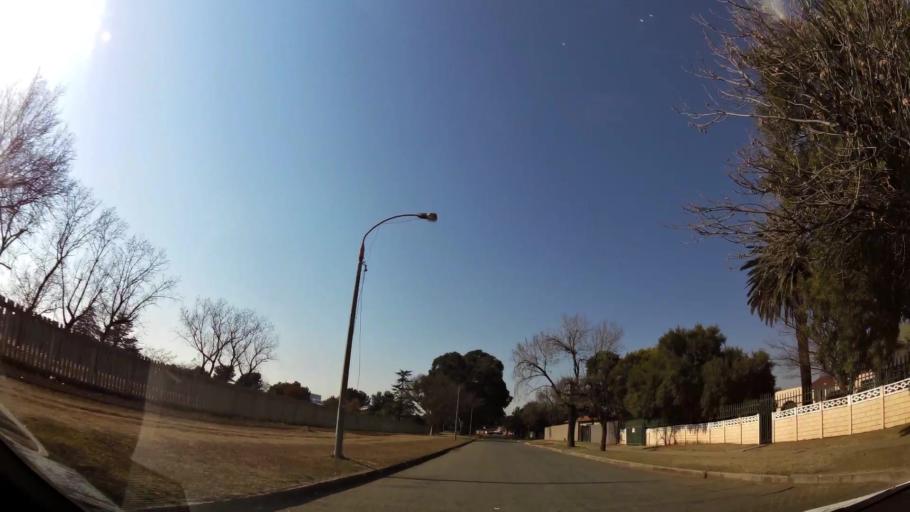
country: ZA
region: Gauteng
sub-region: Ekurhuleni Metropolitan Municipality
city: Boksburg
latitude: -26.2195
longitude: 28.2617
